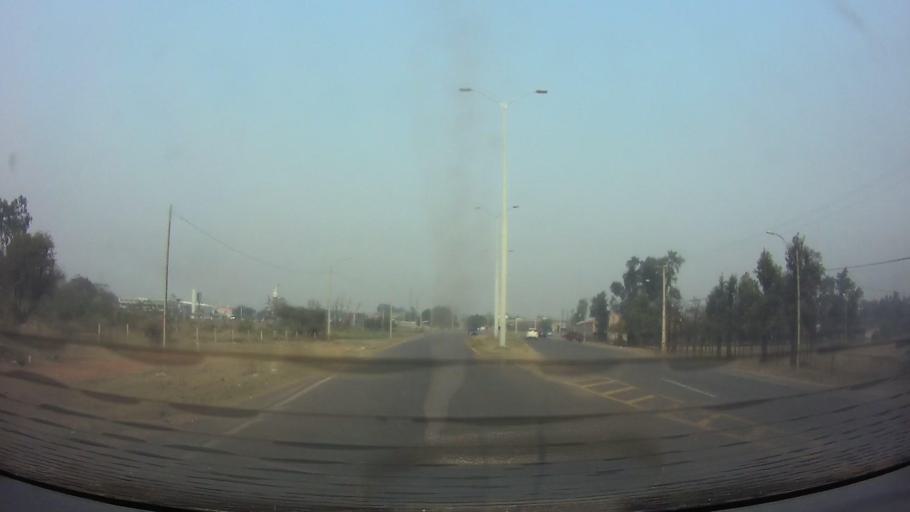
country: PY
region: Central
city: Limpio
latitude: -25.1743
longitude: -57.4871
